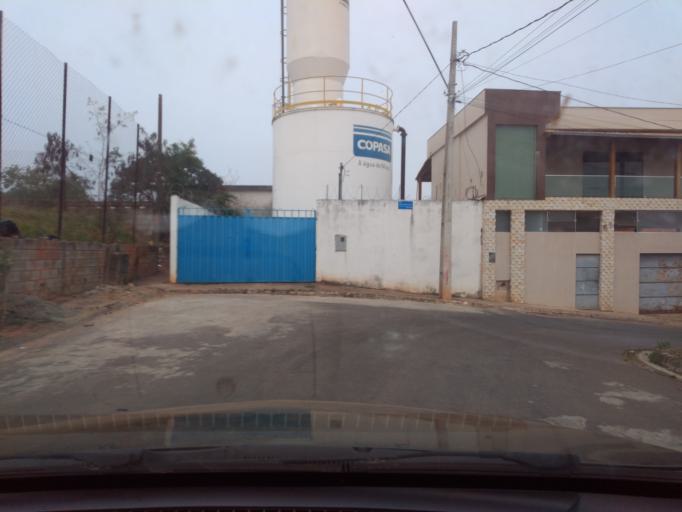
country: BR
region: Minas Gerais
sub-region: Tres Coracoes
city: Tres Coracoes
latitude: -21.6891
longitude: -45.2389
